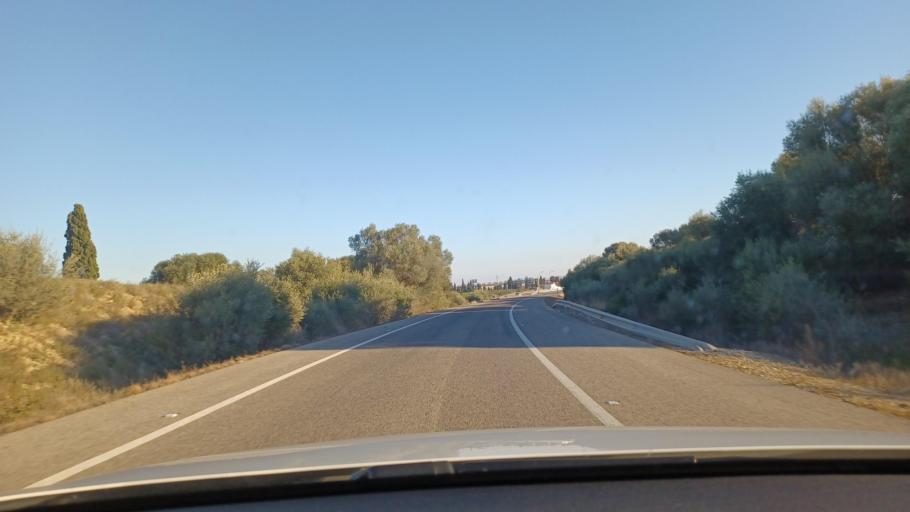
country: ES
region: Catalonia
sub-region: Provincia de Tarragona
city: Amposta
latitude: 40.7304
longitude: 0.5840
